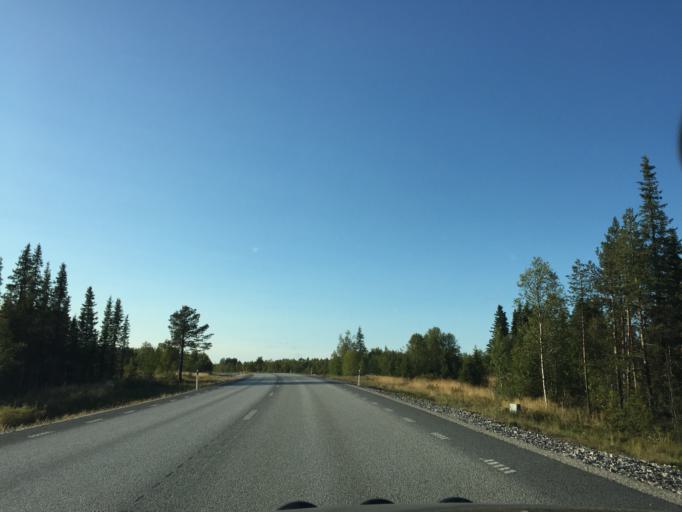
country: SE
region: Norrbotten
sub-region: Gallivare Kommun
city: Malmberget
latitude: 67.6411
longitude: 21.0594
